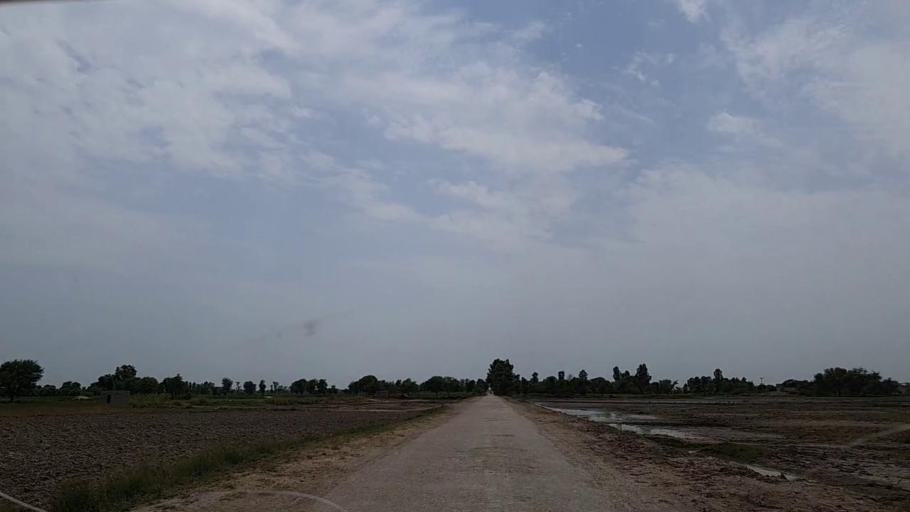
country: PK
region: Sindh
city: Tharu Shah
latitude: 26.9246
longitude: 68.1028
